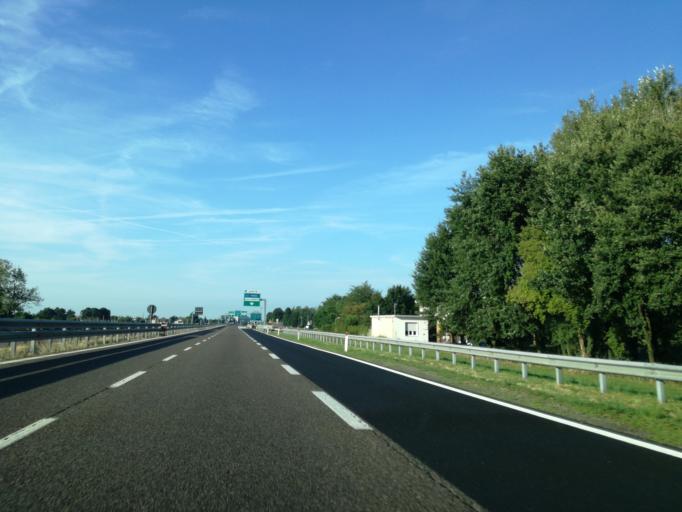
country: IT
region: Lombardy
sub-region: Provincia di Monza e Brianza
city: Agrate Brianza
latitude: 45.5786
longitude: 9.3427
